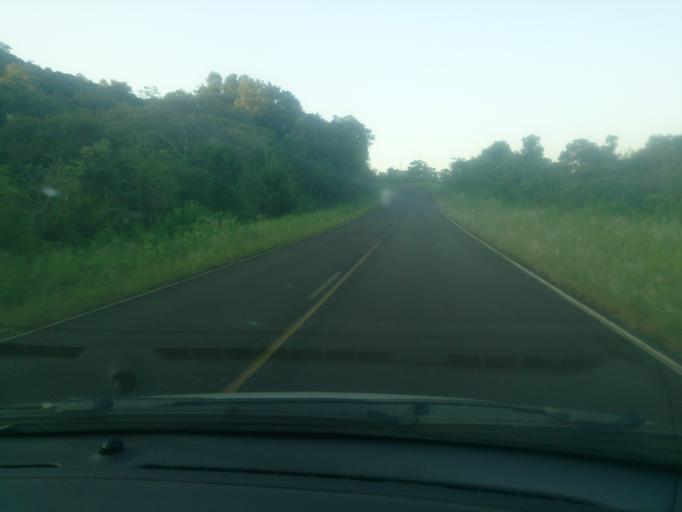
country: AR
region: Misiones
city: Panambi
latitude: -27.6529
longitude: -54.9082
